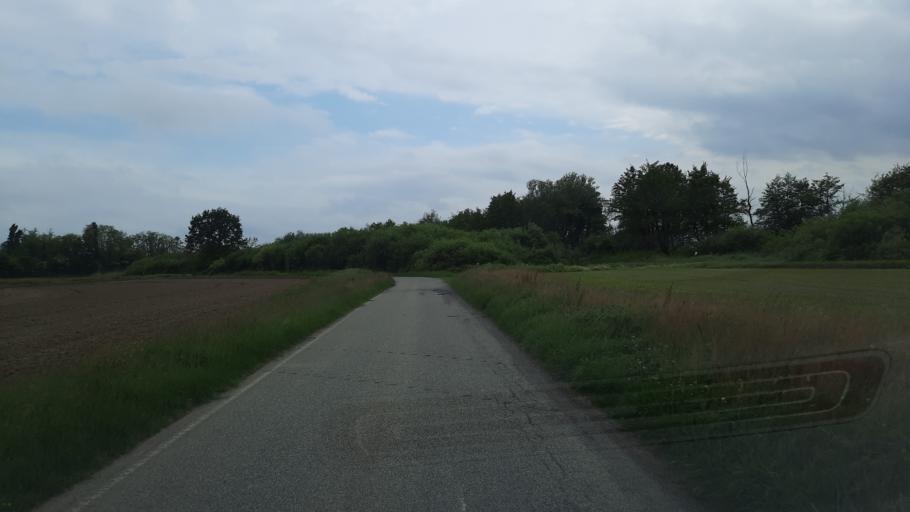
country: IT
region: Lombardy
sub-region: Provincia di Pavia
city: Castelnovetto
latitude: 45.2320
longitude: 8.6019
